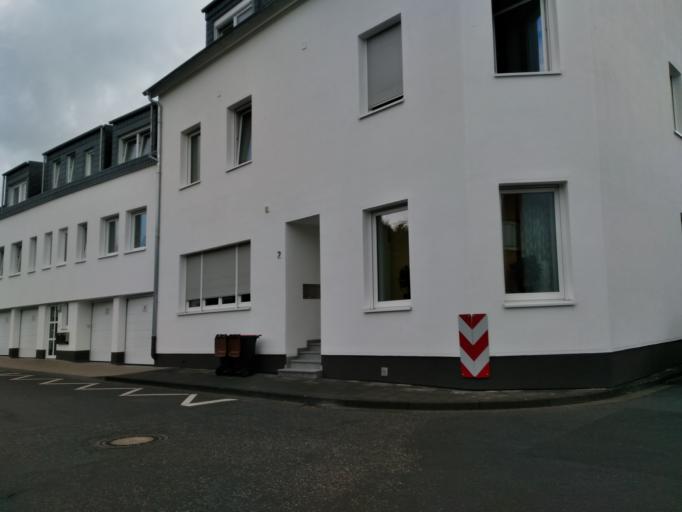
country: DE
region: North Rhine-Westphalia
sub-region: Regierungsbezirk Koln
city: Bad Honnef
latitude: 50.6399
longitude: 7.2347
